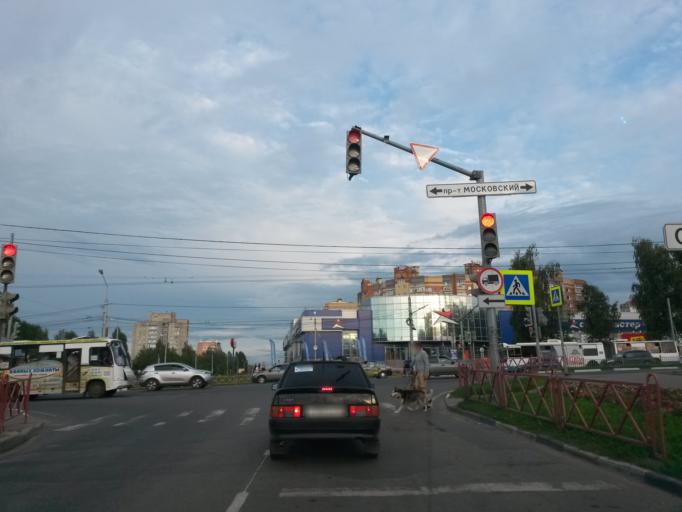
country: RU
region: Jaroslavl
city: Yaroslavl
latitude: 57.5817
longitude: 39.8514
